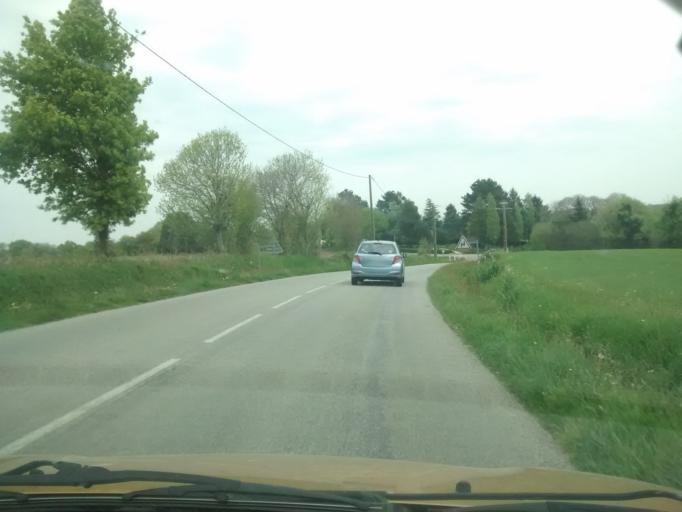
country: FR
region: Brittany
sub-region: Departement du Morbihan
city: Berric
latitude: 47.6469
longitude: -2.4982
